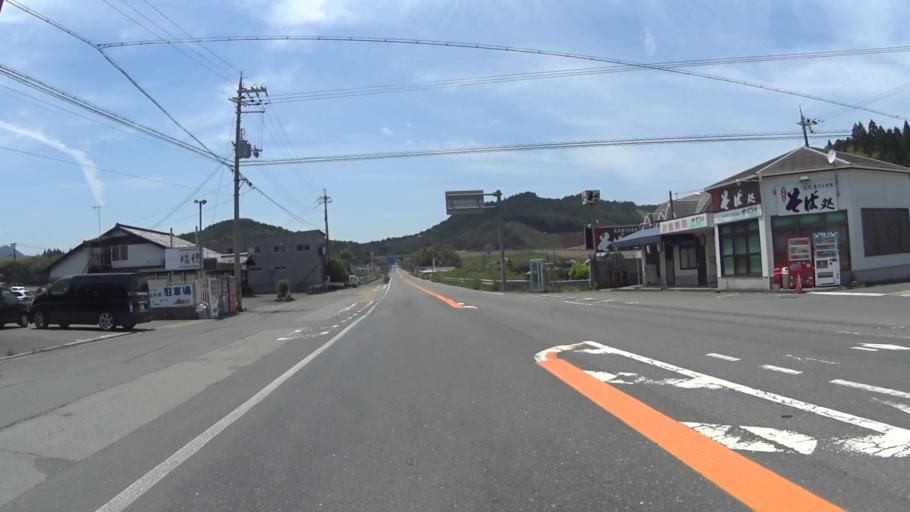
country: JP
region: Kyoto
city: Ayabe
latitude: 35.1826
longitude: 135.3722
